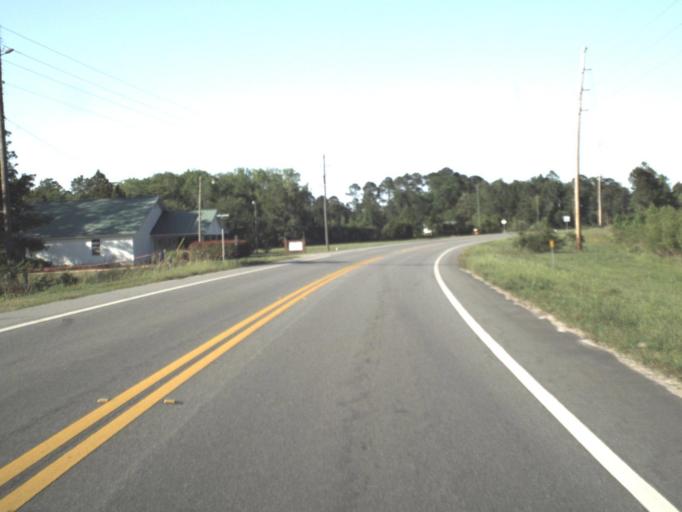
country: US
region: Florida
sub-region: Liberty County
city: Bristol
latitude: 30.3655
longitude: -84.8170
